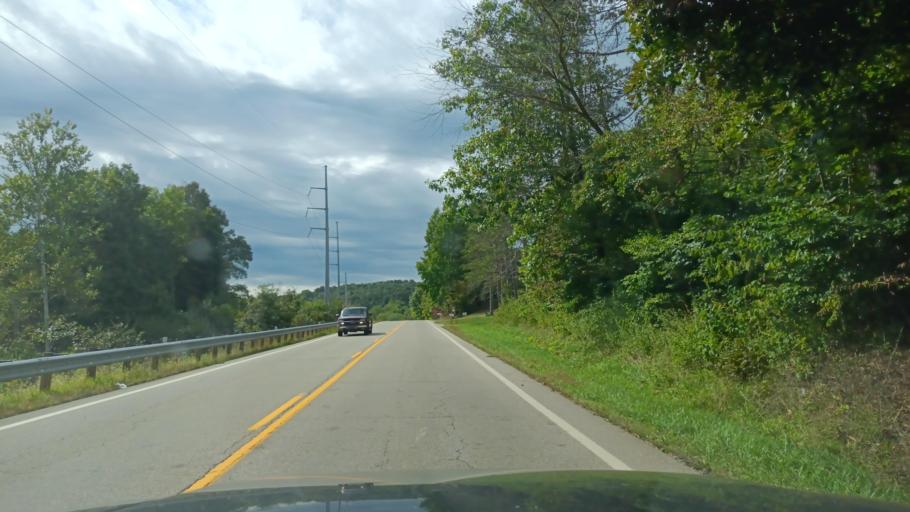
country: US
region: Ohio
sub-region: Vinton County
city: McArthur
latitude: 39.2409
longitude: -82.3623
